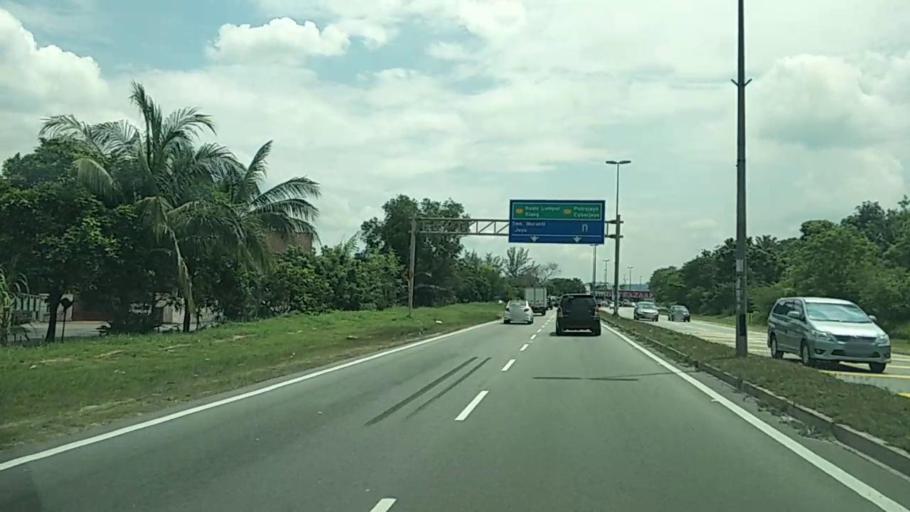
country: MY
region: Selangor
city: Subang Jaya
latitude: 2.9761
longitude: 101.6119
